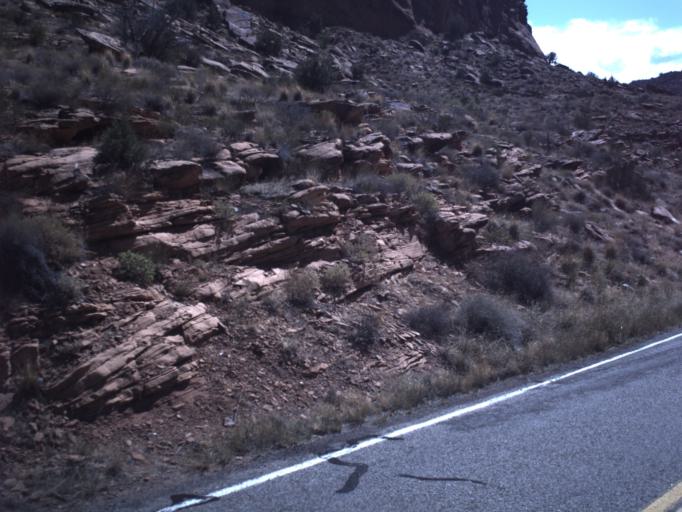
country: US
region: Utah
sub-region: Grand County
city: Moab
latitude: 38.8018
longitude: -109.3121
